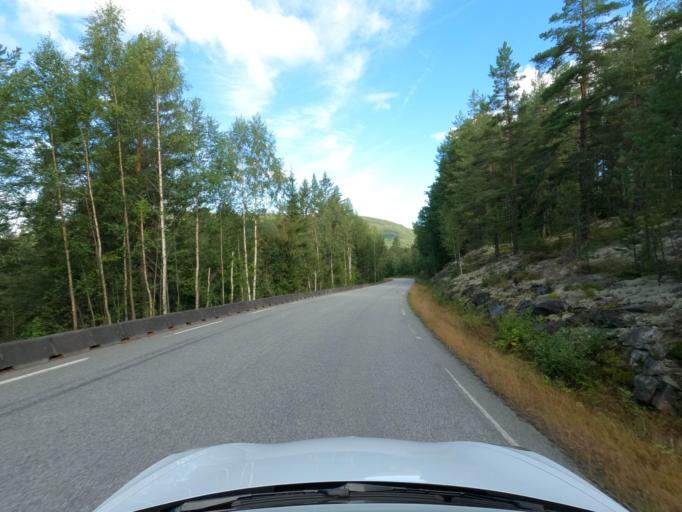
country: NO
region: Telemark
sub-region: Tinn
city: Rjukan
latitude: 59.9890
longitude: 8.8464
